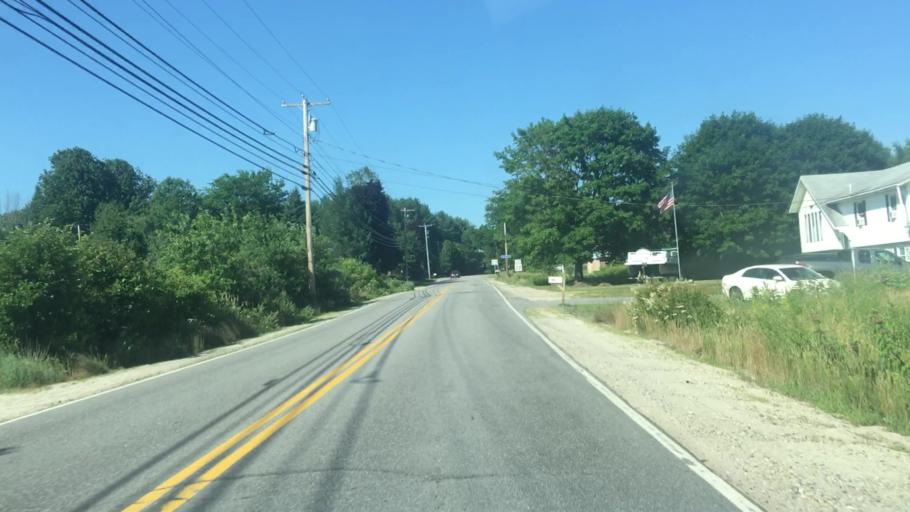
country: US
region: Maine
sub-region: York County
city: Hollis Center
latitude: 43.6770
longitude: -70.5917
